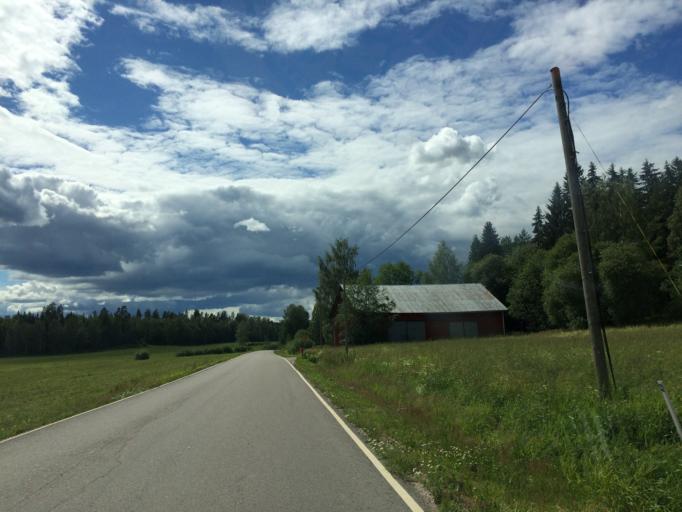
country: FI
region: Haeme
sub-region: Haemeenlinna
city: Janakkala
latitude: 60.8409
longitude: 24.5394
